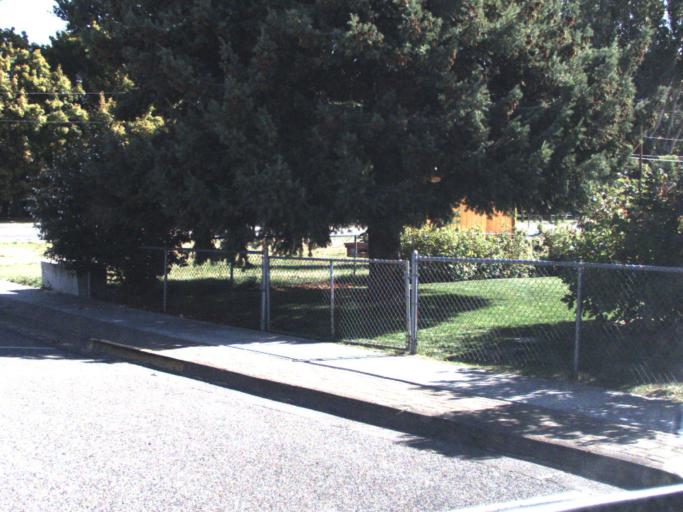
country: US
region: Washington
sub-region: Walla Walla County
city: Waitsburg
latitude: 46.2701
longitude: -118.1536
